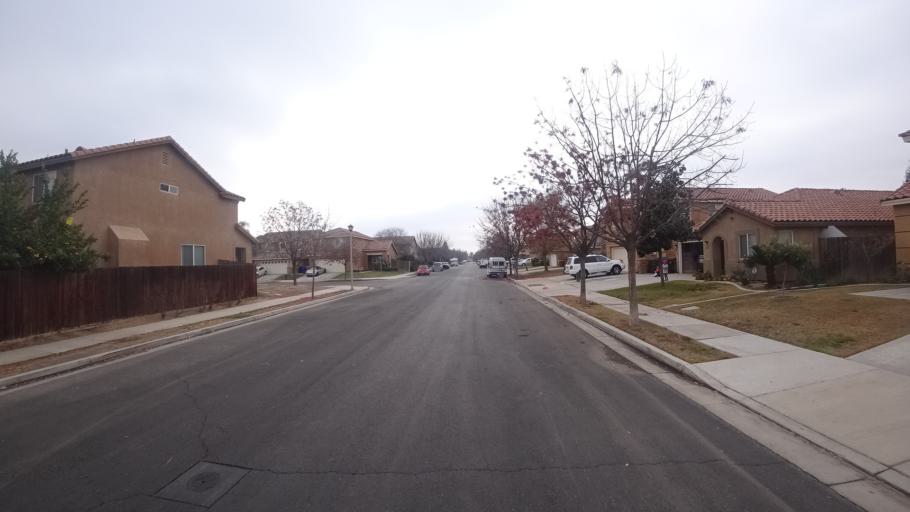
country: US
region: California
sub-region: Kern County
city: Greenfield
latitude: 35.2996
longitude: -119.0766
